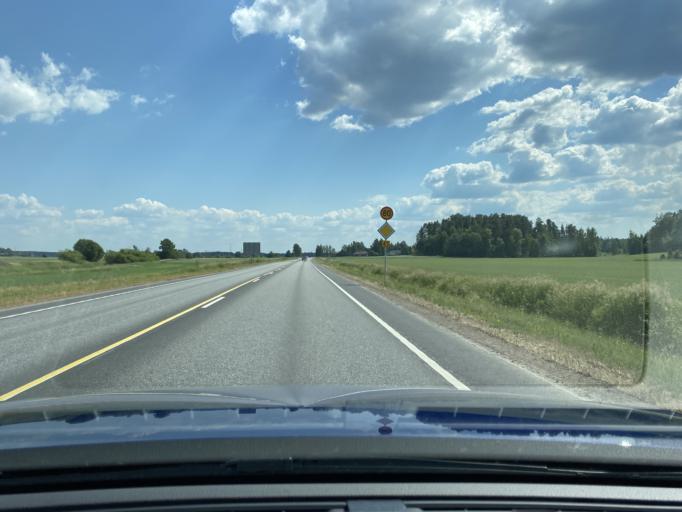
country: FI
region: Satakunta
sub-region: Rauma
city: Eura
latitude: 61.1551
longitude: 22.0940
